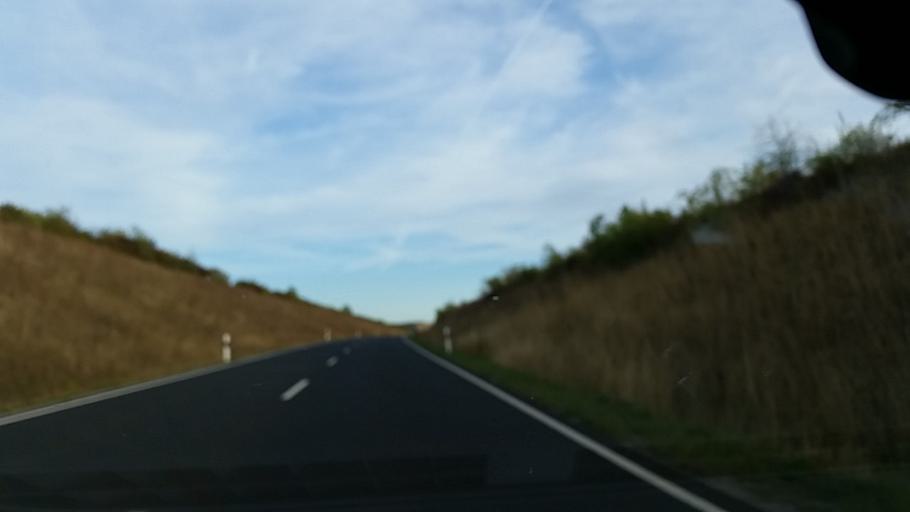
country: DE
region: Bavaria
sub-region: Regierungsbezirk Unterfranken
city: Mellrichstadt
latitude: 50.4399
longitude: 10.3186
